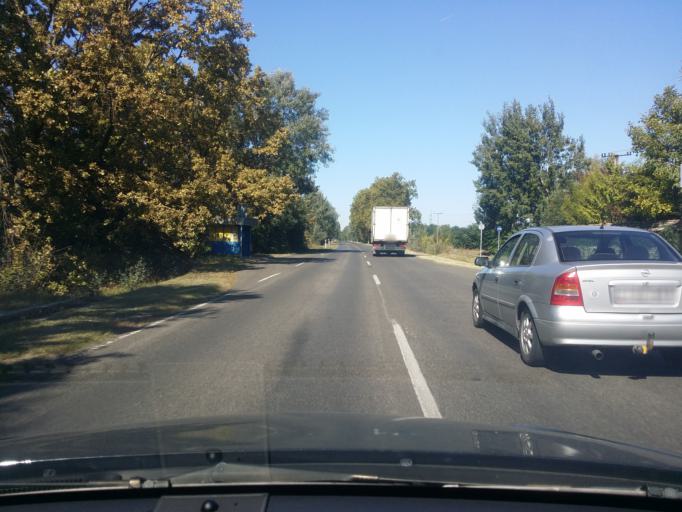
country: HU
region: Csongrad
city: Balastya
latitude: 46.4481
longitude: 19.9986
